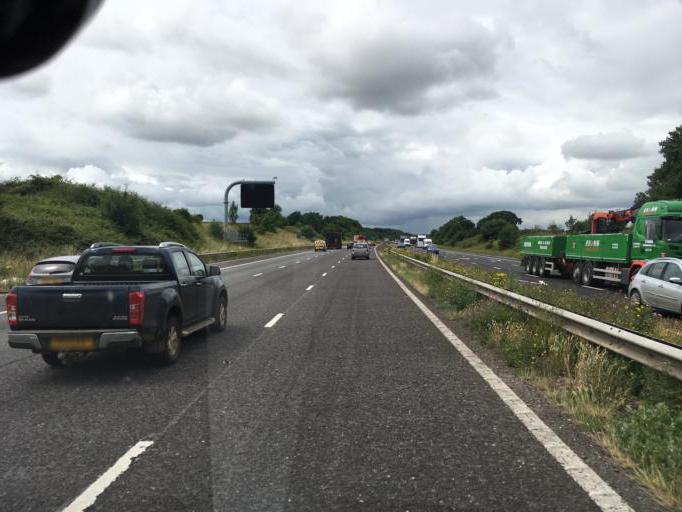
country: GB
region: England
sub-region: Gloucestershire
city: Gloucester
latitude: 51.8069
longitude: -2.2531
